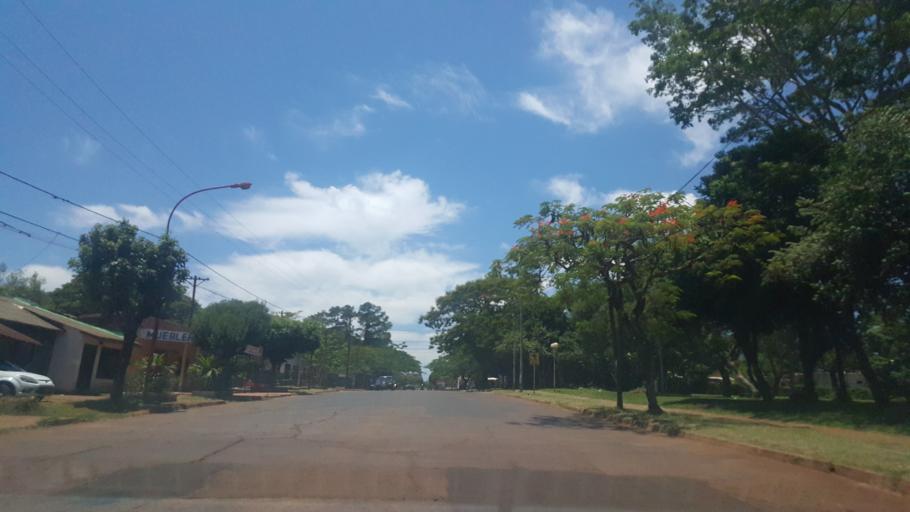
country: AR
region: Misiones
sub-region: Departamento de Capital
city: Posadas
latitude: -27.3670
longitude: -55.9337
